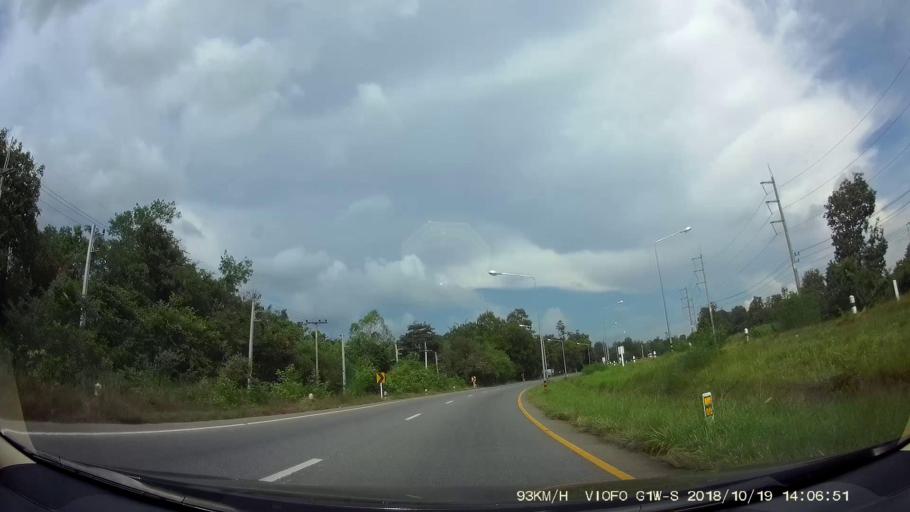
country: TH
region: Chaiyaphum
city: Chaiyaphum
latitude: 15.8913
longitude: 102.1093
